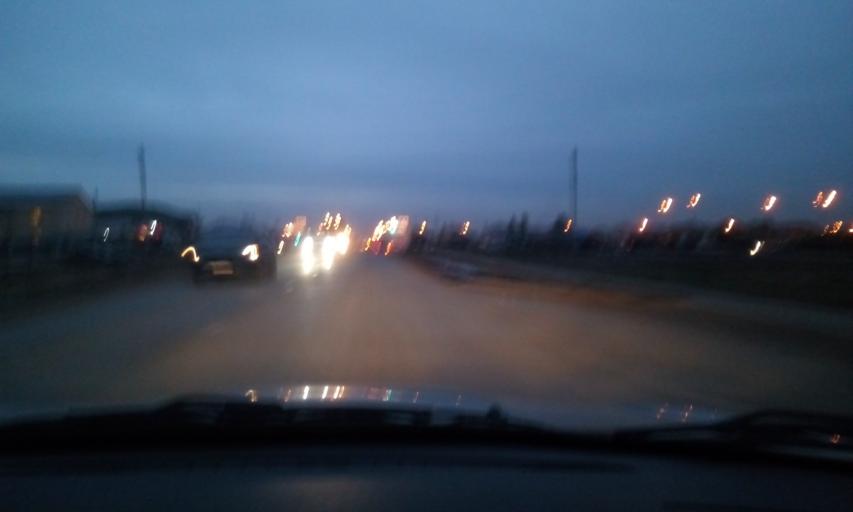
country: KZ
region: Astana Qalasy
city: Astana
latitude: 51.1363
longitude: 71.5242
